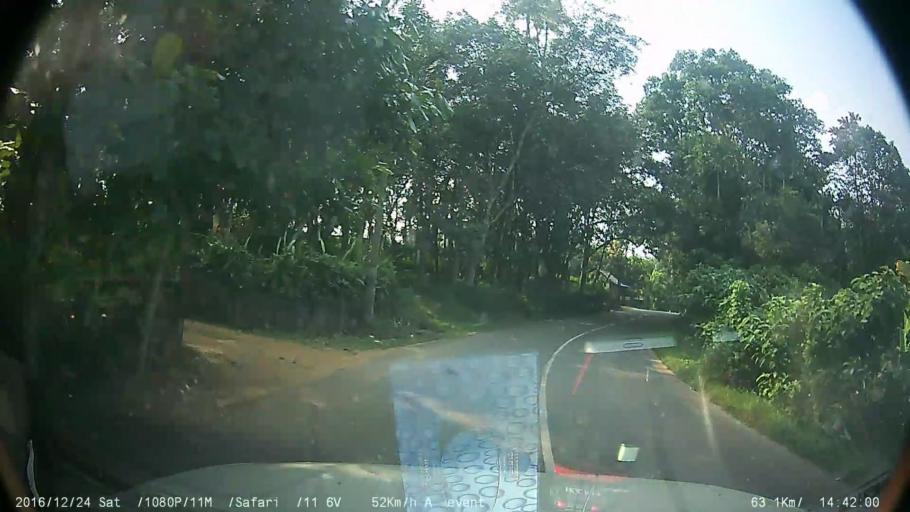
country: IN
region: Kerala
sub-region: Kottayam
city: Lalam
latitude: 9.7780
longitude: 76.7288
